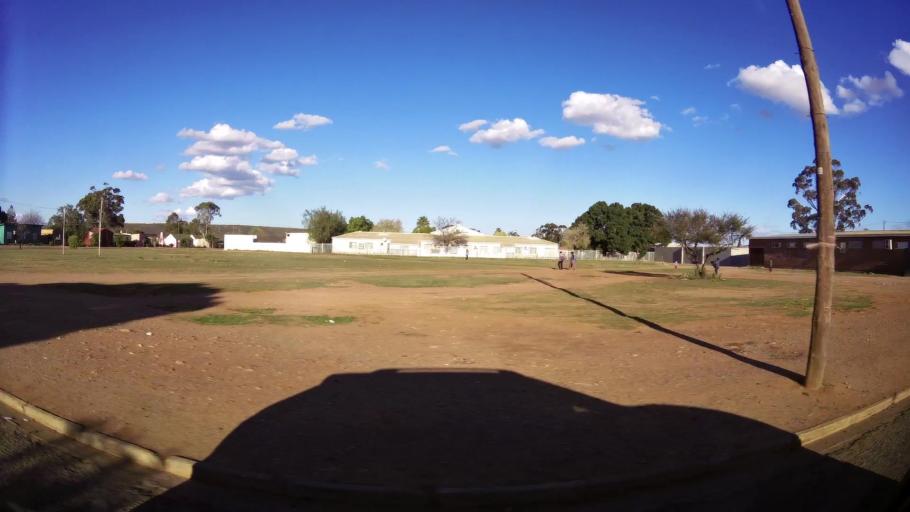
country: ZA
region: Western Cape
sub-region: Eden District Municipality
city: Riversdale
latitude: -34.1015
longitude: 20.9615
